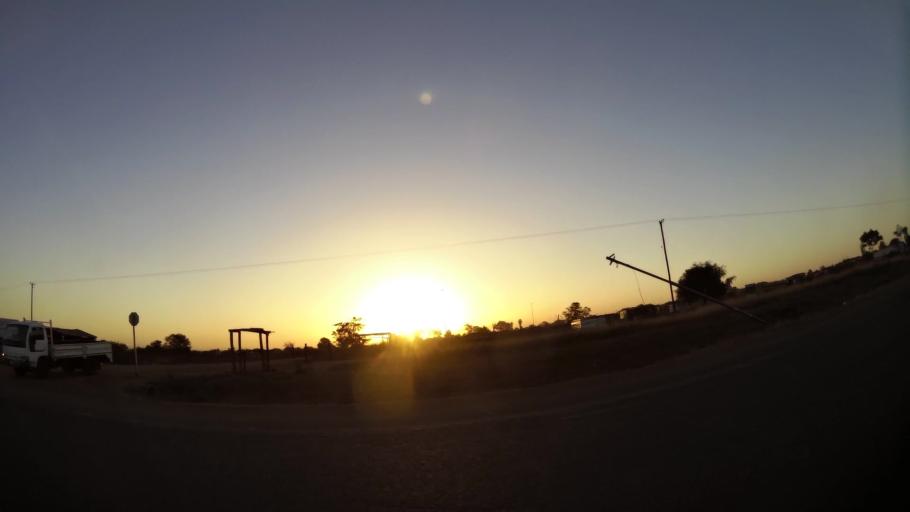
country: ZA
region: North-West
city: Ga-Rankuwa
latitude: -25.5710
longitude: 28.0527
